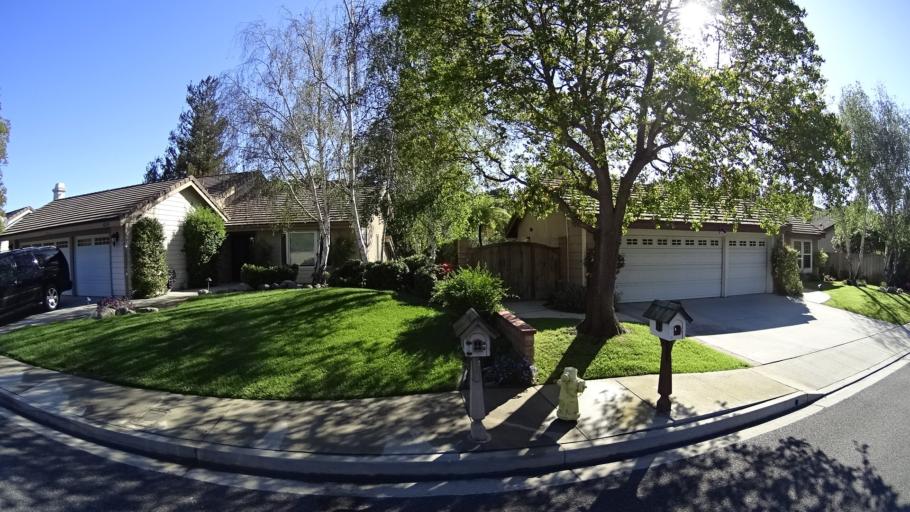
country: US
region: California
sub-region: Ventura County
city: Casa Conejo
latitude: 34.1865
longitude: -118.9081
